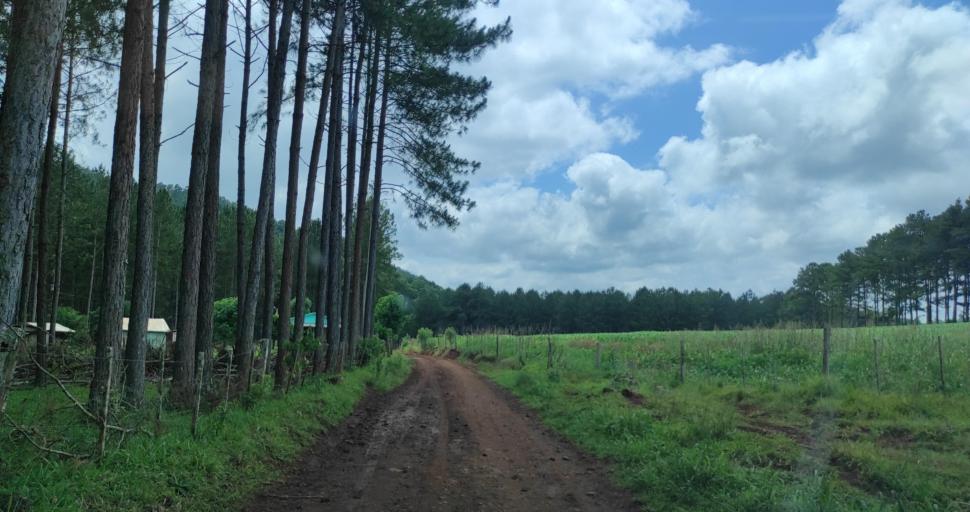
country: AR
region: Misiones
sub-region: Departamento de Veinticinco de Mayo
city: Veinticinco de Mayo
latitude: -27.4200
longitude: -54.7061
